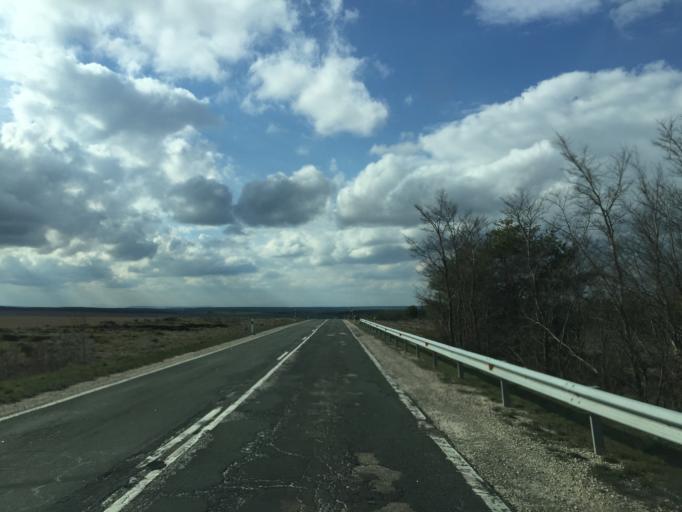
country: ES
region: Castille and Leon
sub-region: Provincia de Burgos
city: Tubilla del Agua
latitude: 42.6534
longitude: -3.7642
